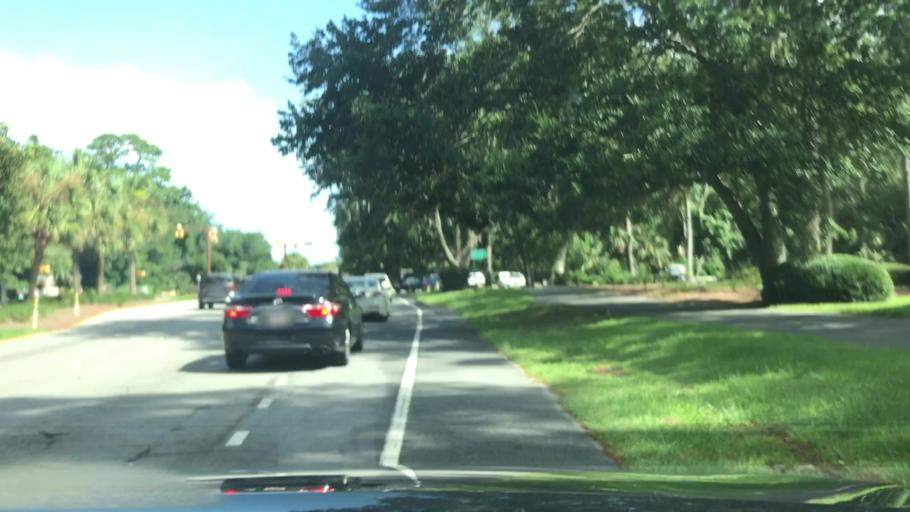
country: US
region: South Carolina
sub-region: Beaufort County
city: Hilton Head Island
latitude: 32.1485
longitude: -80.7569
